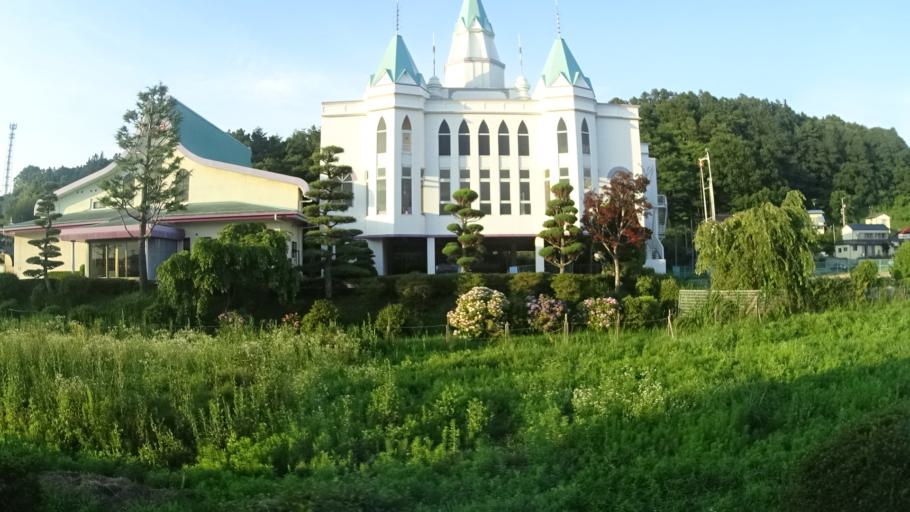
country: JP
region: Fukushima
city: Funehikimachi-funehiki
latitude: 37.4436
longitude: 140.5740
